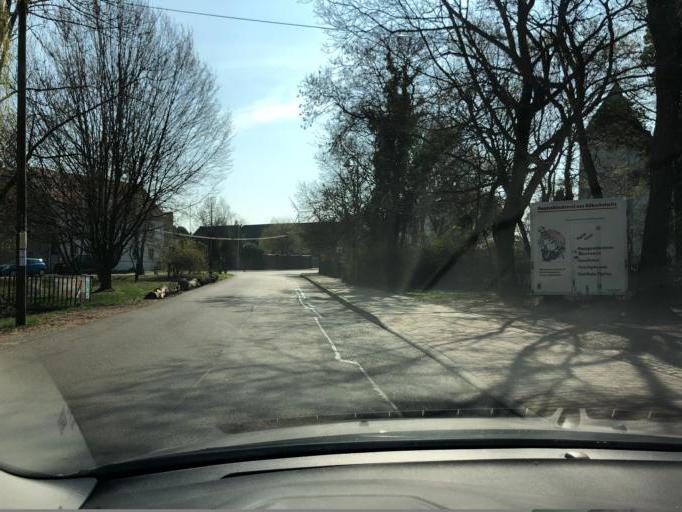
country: DE
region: Saxony
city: Rackwitz
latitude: 51.4219
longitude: 12.4211
